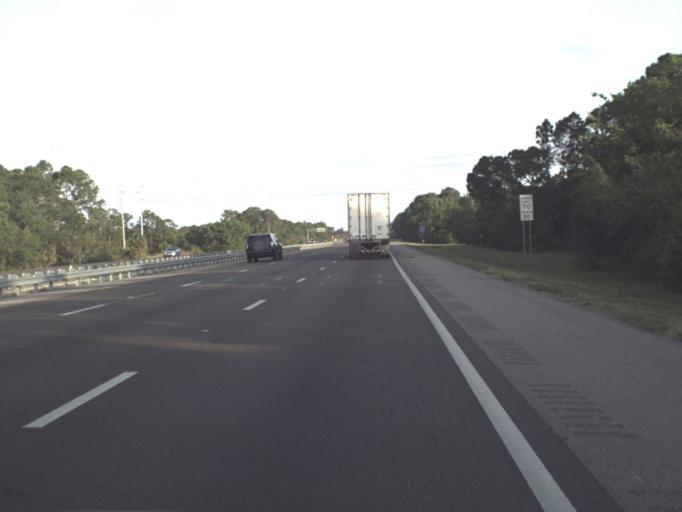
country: US
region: Florida
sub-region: Brevard County
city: Port Saint John
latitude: 28.4929
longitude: -80.8319
